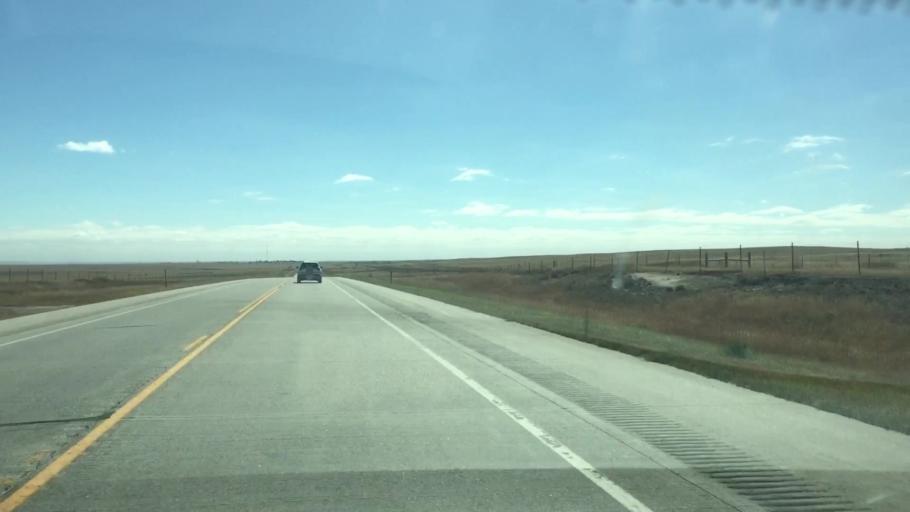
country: US
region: Colorado
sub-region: Lincoln County
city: Hugo
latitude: 39.1755
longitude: -103.5390
